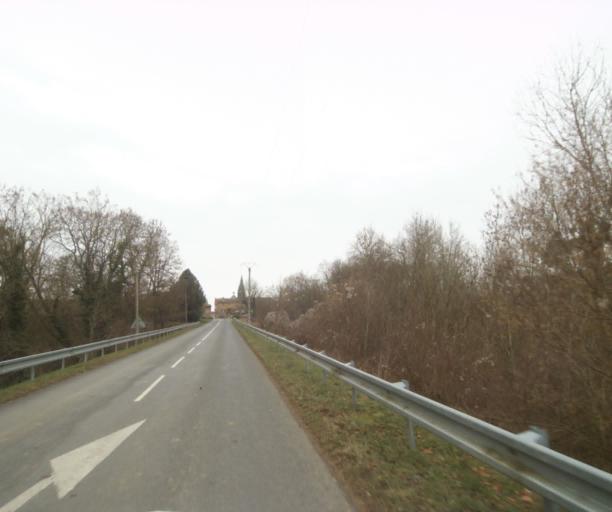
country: FR
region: Champagne-Ardenne
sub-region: Departement de la Haute-Marne
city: Villiers-en-Lieu
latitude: 48.6405
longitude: 4.7677
